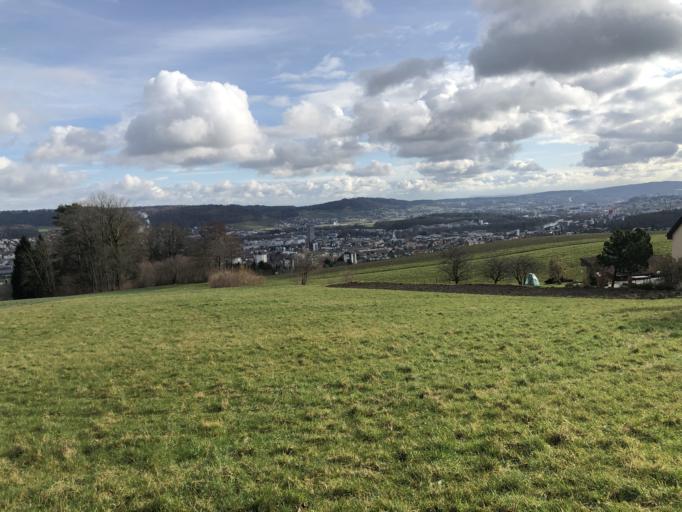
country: CH
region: Zurich
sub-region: Bezirk Dietikon
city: Dietikon / Almend
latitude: 47.3985
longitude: 8.3765
